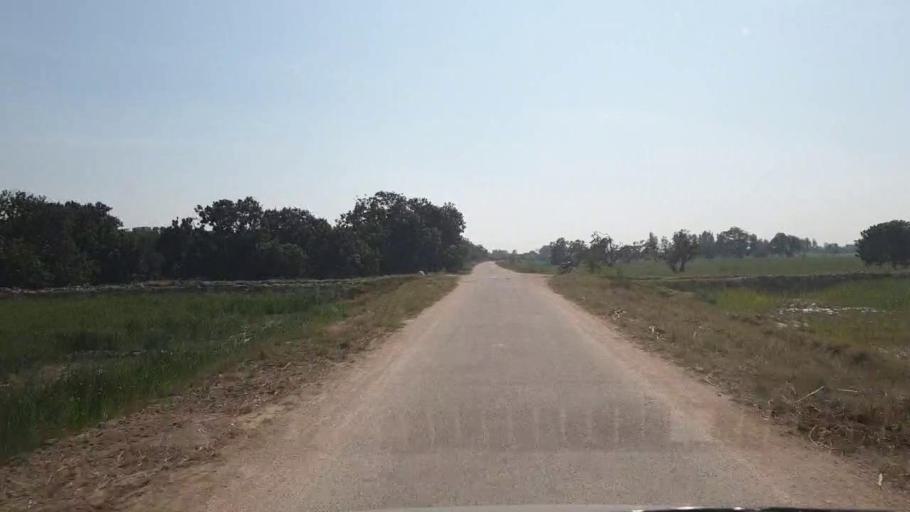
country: PK
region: Sindh
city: Chambar
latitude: 25.3800
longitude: 68.8058
